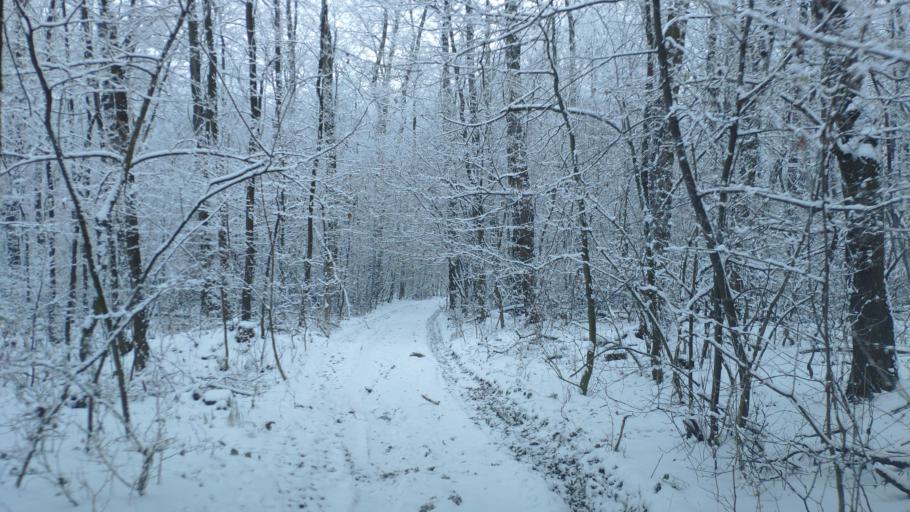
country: SK
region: Kosicky
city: Kosice
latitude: 48.6449
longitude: 21.1834
